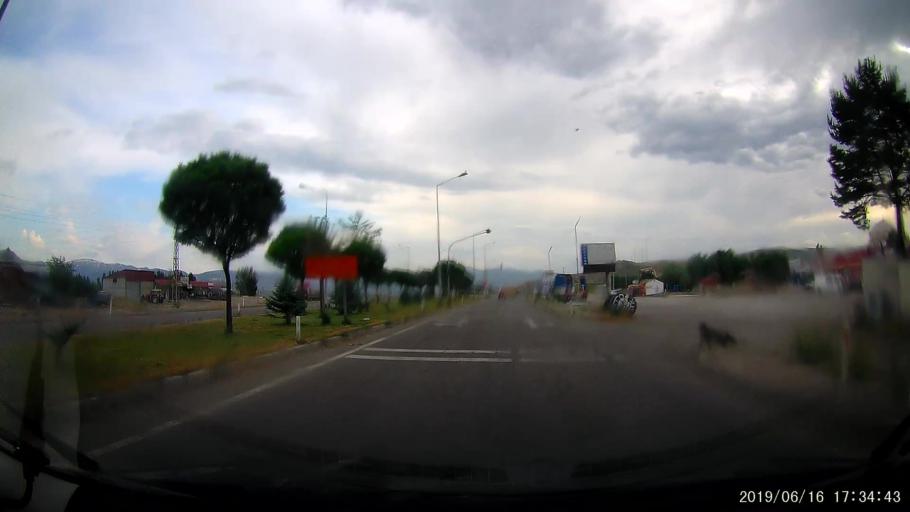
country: TR
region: Erzincan
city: Tercan
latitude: 39.7395
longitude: 40.2666
